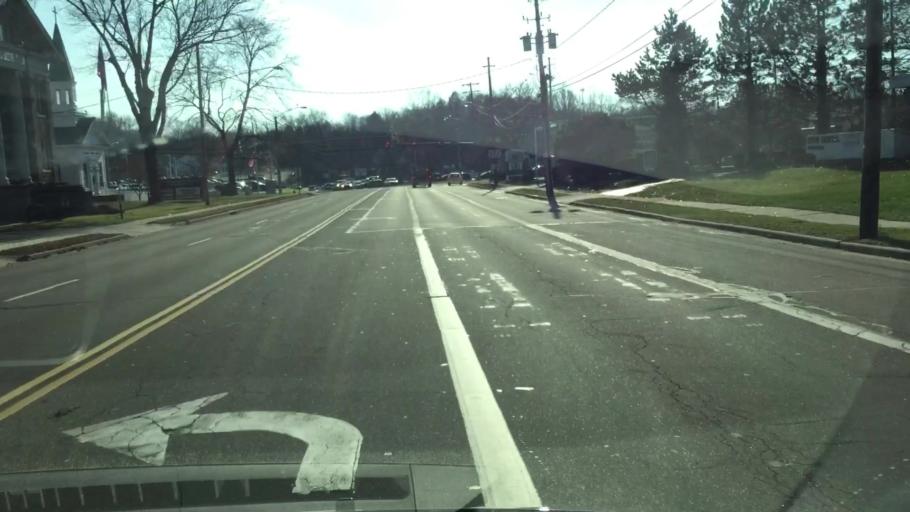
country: US
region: Ohio
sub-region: Summit County
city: Stow
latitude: 41.1606
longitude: -81.4404
